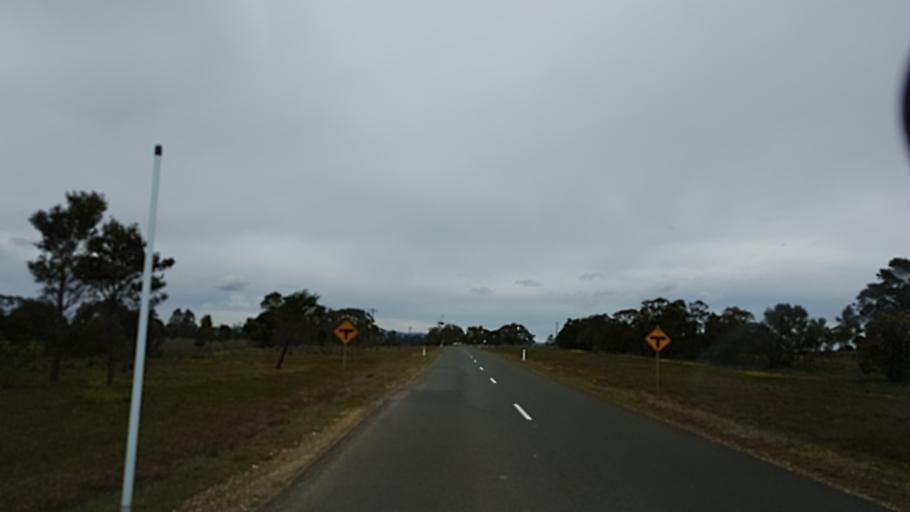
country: AU
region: Victoria
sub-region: Moorabool
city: Bacchus Marsh
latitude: -37.6263
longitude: 144.2093
